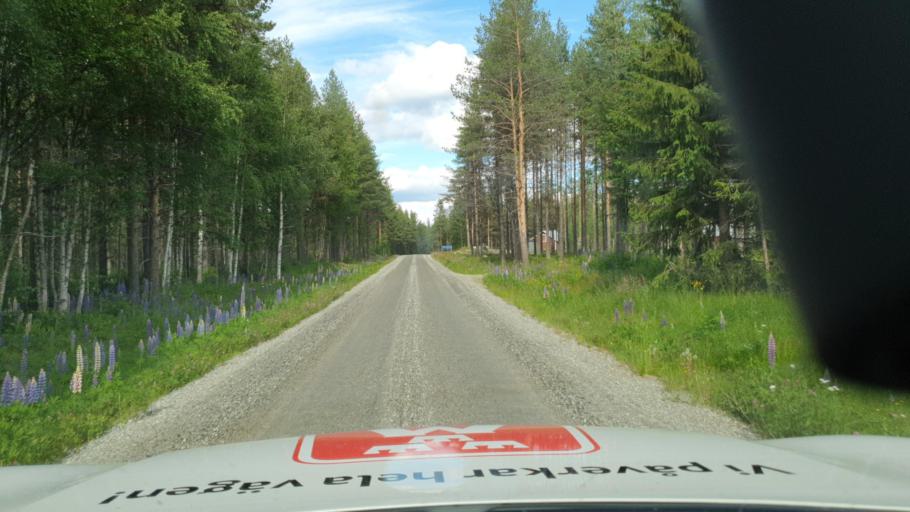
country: SE
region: Vaesterbotten
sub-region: Asele Kommun
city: Insjon
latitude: 64.2370
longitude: 17.9131
